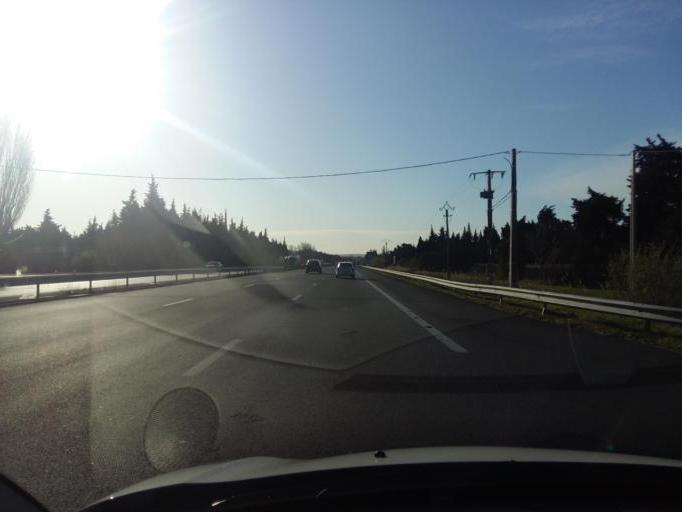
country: FR
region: Provence-Alpes-Cote d'Azur
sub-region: Departement des Bouches-du-Rhone
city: Senas
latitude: 43.7440
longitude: 5.0792
